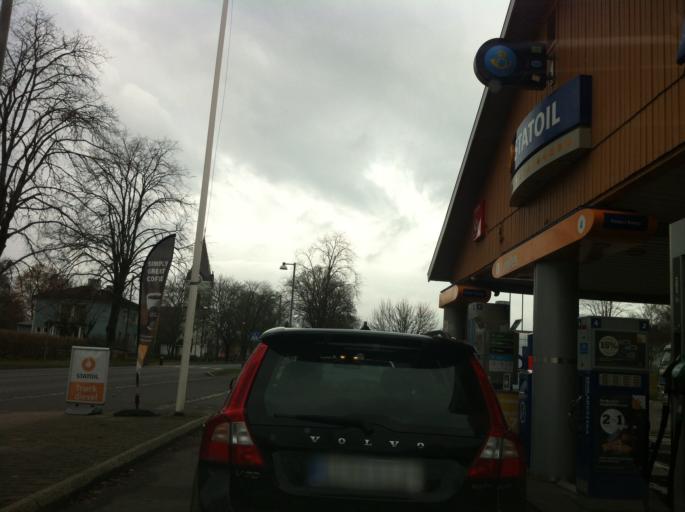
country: SE
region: Joenkoeping
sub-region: Savsjo Kommun
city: Vrigstad
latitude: 57.3595
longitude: 14.4880
